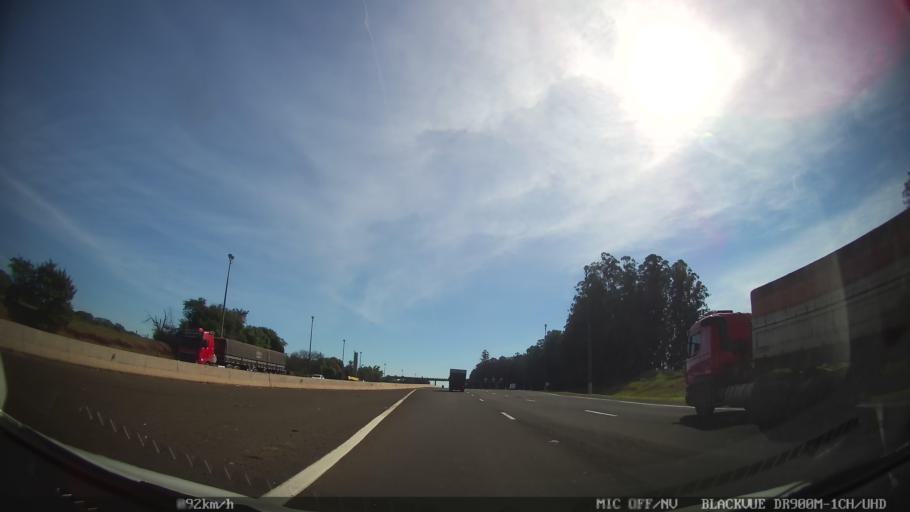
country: BR
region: Sao Paulo
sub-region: Pirassununga
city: Pirassununga
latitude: -21.9605
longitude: -47.4586
